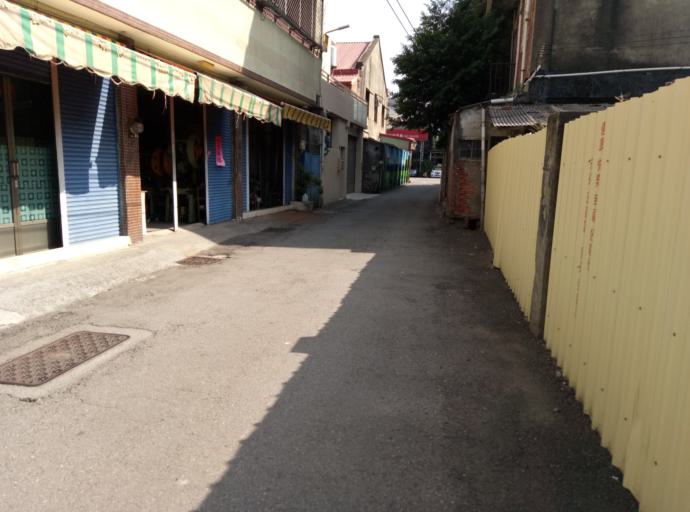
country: TW
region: Taiwan
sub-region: Changhua
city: Chang-hua
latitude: 24.0855
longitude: 120.5552
